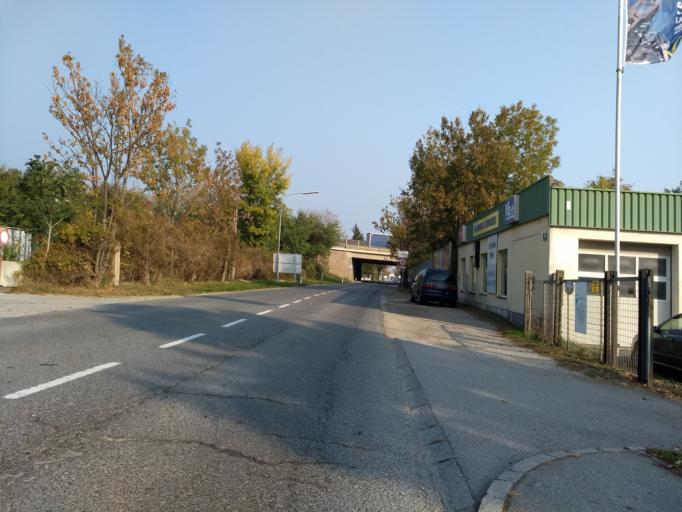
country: AT
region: Lower Austria
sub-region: Politischer Bezirk Modling
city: Brunn am Gebirge
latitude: 48.1150
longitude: 16.2886
